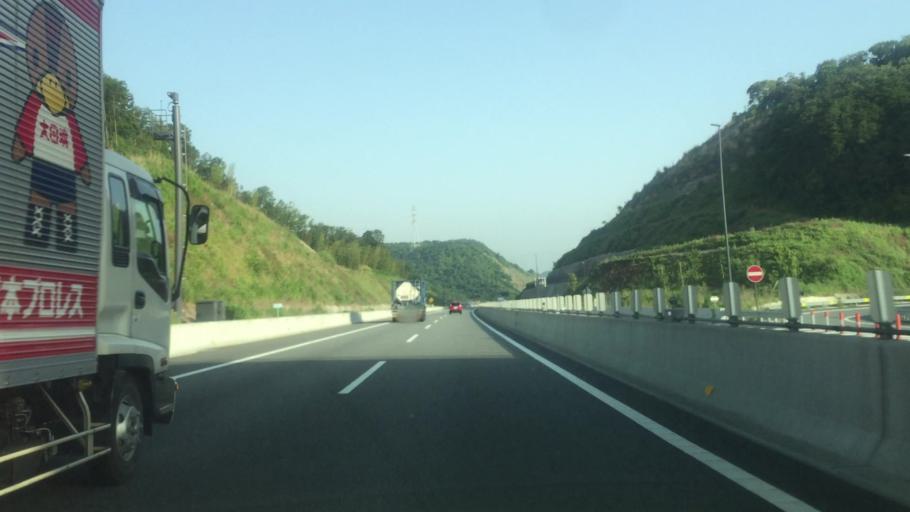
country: JP
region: Aichi
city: Gamagori
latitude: 34.9196
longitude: 137.2765
